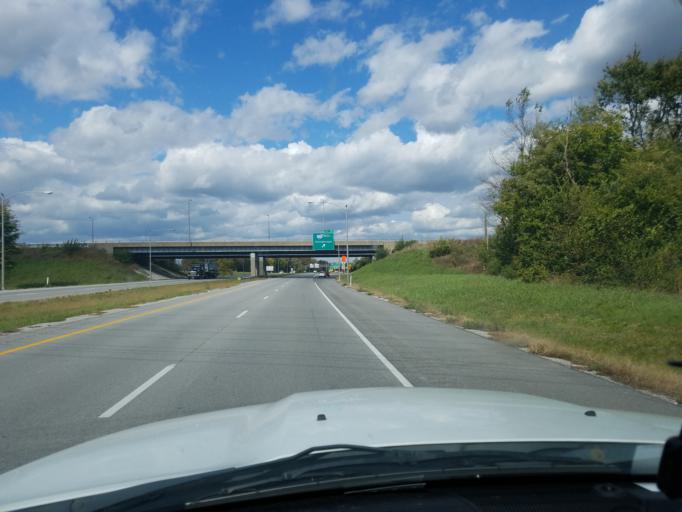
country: US
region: Kentucky
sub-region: Daviess County
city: Owensboro
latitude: 37.7647
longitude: -87.1629
